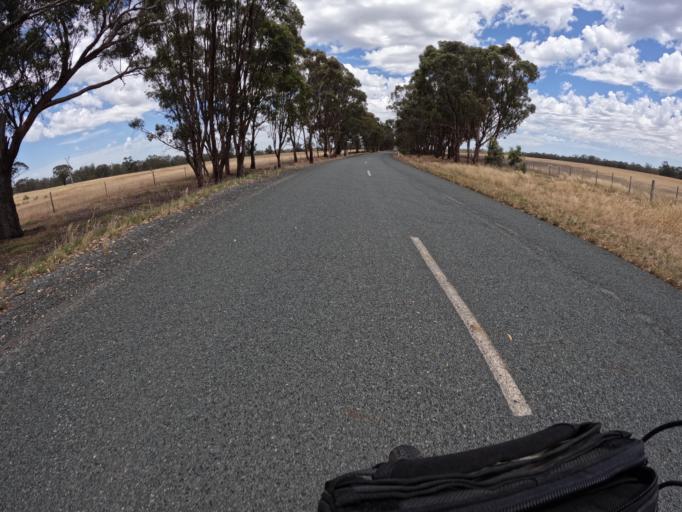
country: AU
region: Victoria
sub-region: Greater Shepparton
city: Shepparton
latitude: -36.6788
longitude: 145.1964
